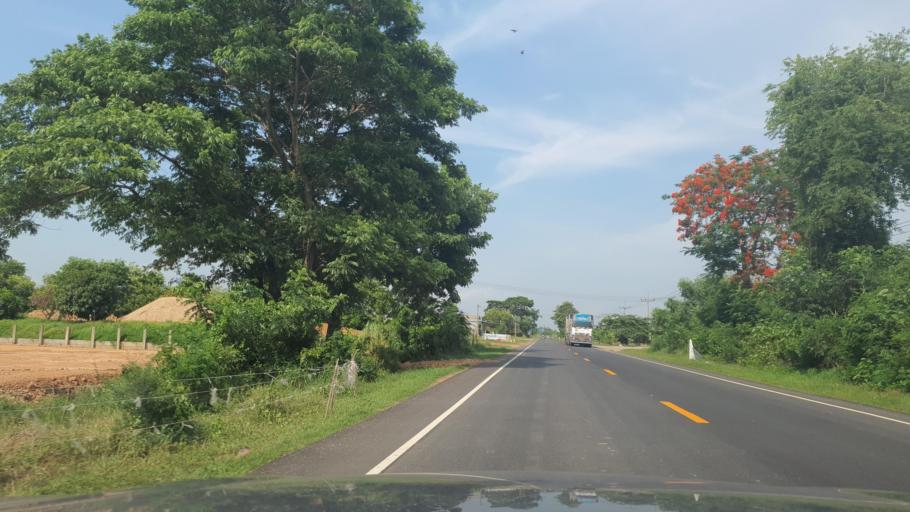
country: TH
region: Sukhothai
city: Si Samrong
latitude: 17.1705
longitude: 99.8418
